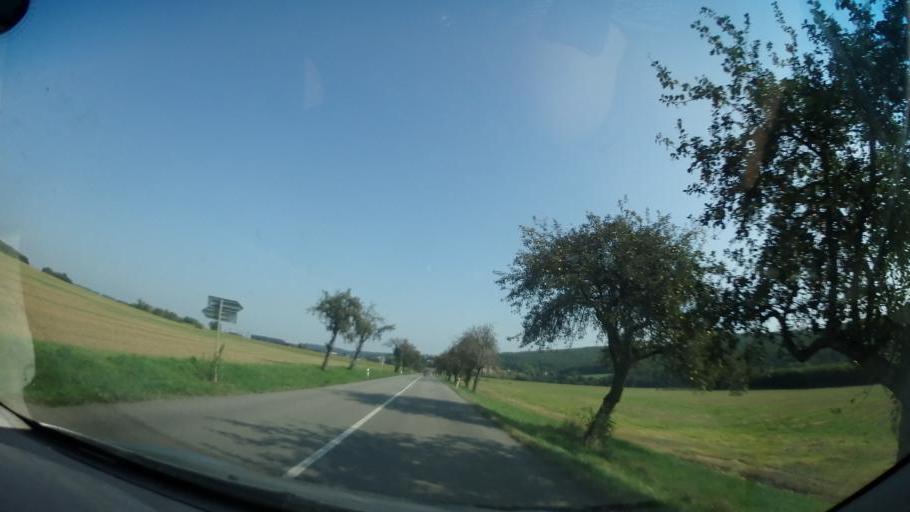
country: CZ
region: South Moravian
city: Kurim
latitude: 49.2547
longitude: 16.5246
